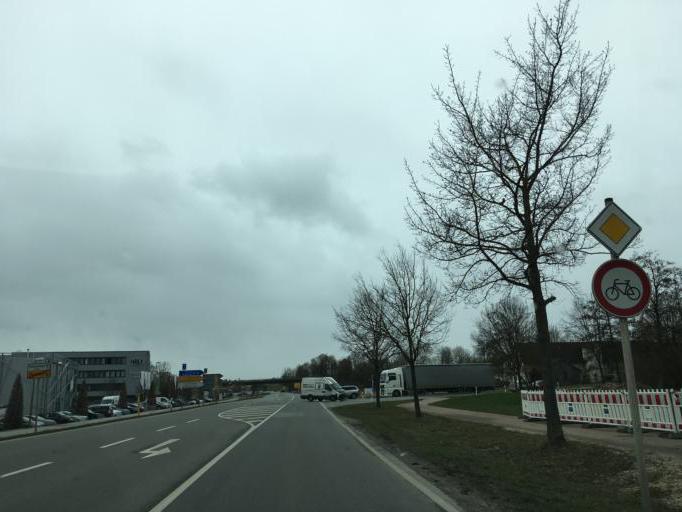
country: DE
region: Bavaria
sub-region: Lower Bavaria
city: Mainburg
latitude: 48.6324
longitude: 11.7782
